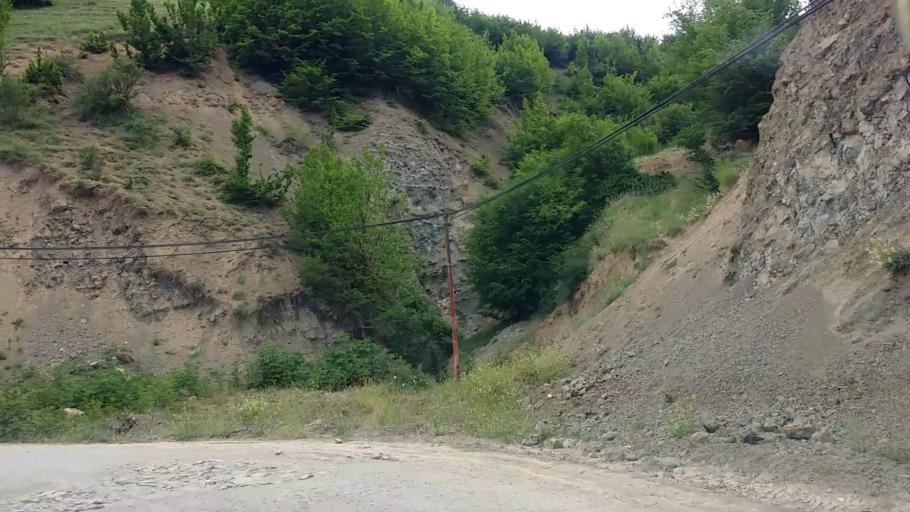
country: IR
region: Mazandaran
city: Chalus
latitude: 36.5526
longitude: 51.2688
